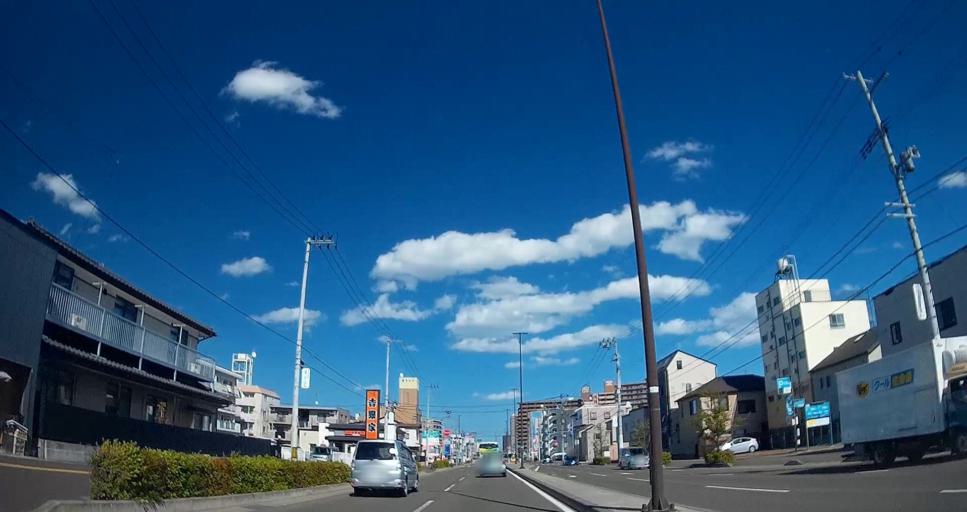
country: JP
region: Miyagi
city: Sendai-shi
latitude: 38.2520
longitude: 140.9117
